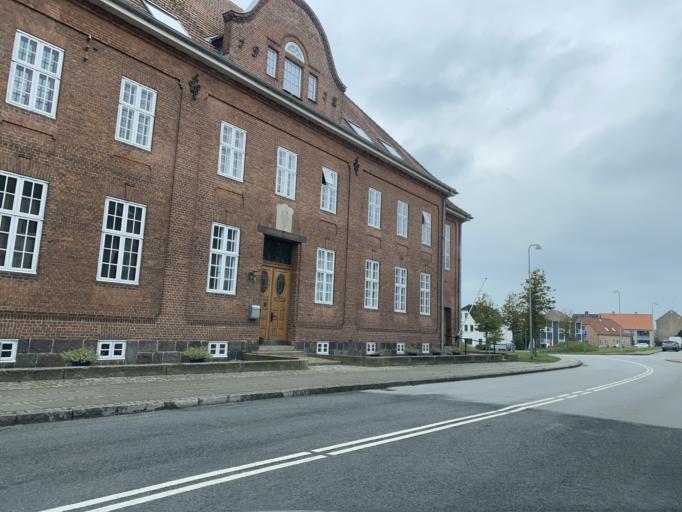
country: DK
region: South Denmark
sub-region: Haderslev Kommune
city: Haderslev
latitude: 55.2496
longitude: 9.4981
